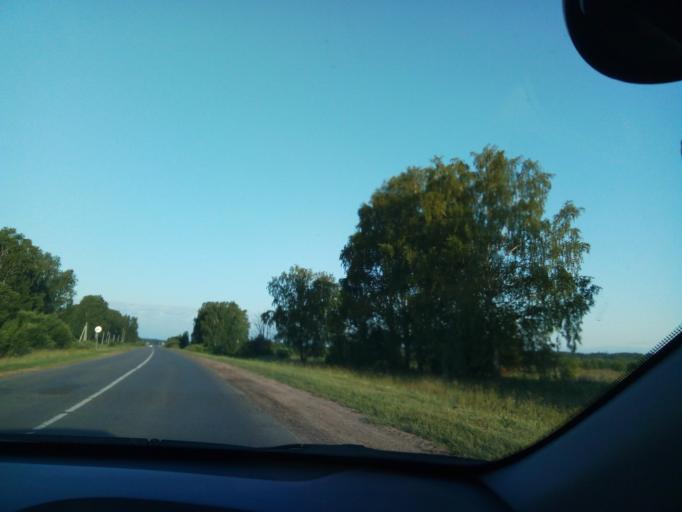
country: RU
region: Nizjnij Novgorod
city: Satis
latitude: 54.9385
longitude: 43.2466
